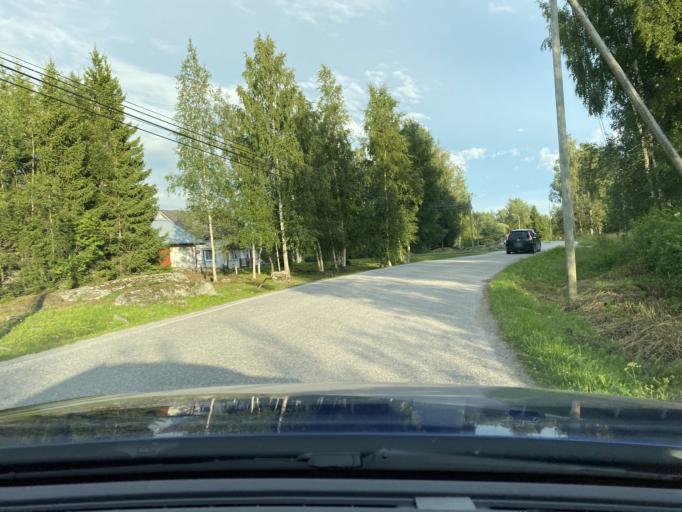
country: FI
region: Ostrobothnia
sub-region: Vaasa
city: Korsnaes
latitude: 62.9737
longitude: 21.1777
